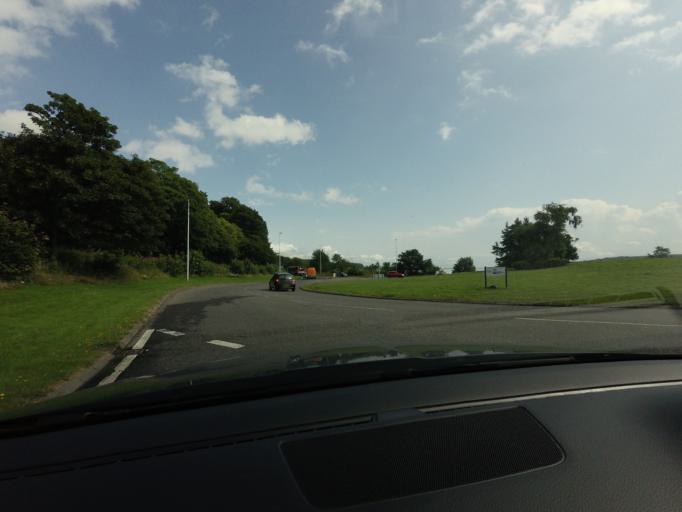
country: GB
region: Scotland
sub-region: Highland
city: Evanton
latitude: 57.6278
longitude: -4.3679
